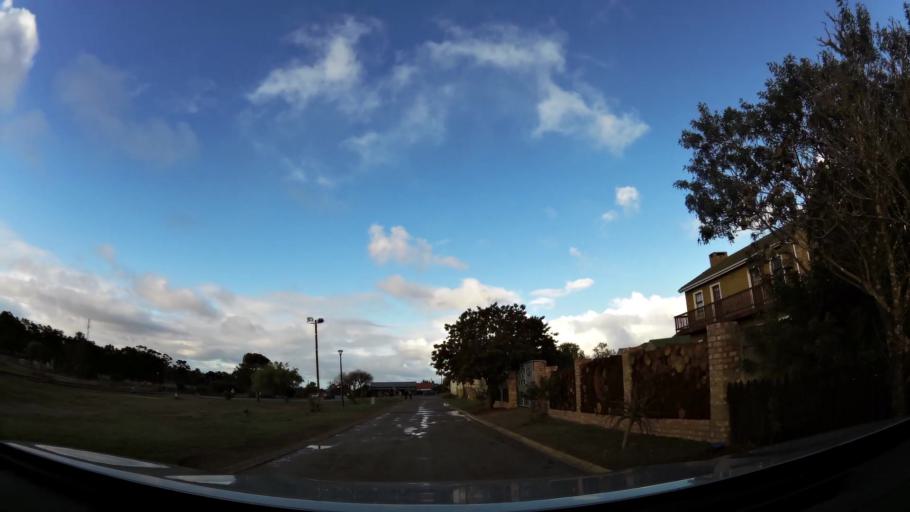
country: ZA
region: Western Cape
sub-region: Eden District Municipality
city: Riversdale
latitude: -34.2021
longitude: 21.5840
